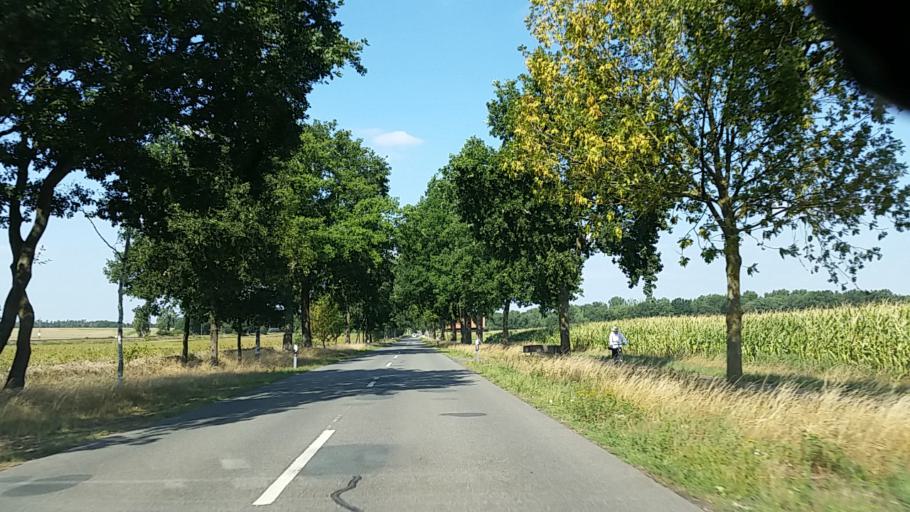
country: DE
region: Lower Saxony
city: Bad Bevensen
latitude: 53.0970
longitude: 10.5582
